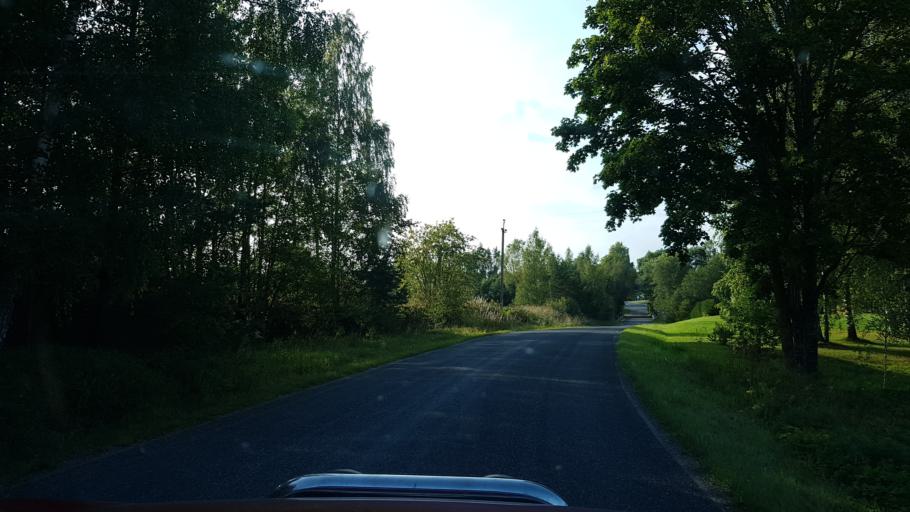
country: EE
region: Polvamaa
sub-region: Polva linn
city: Polva
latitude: 58.1226
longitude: 26.9607
